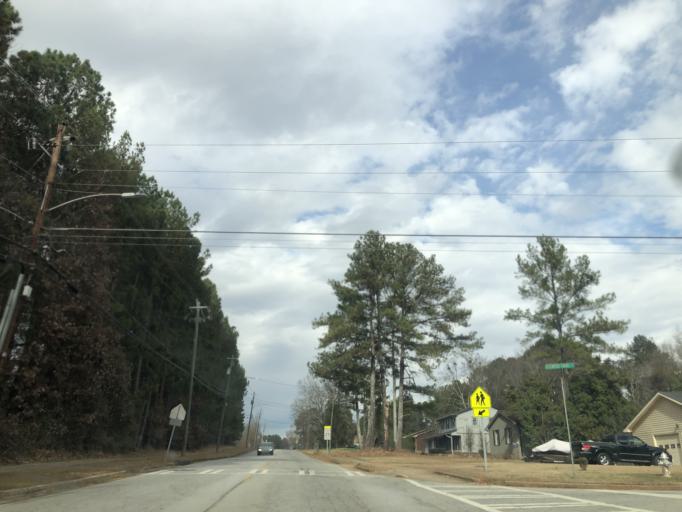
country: US
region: Georgia
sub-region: DeKalb County
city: Panthersville
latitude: 33.6769
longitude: -84.2151
